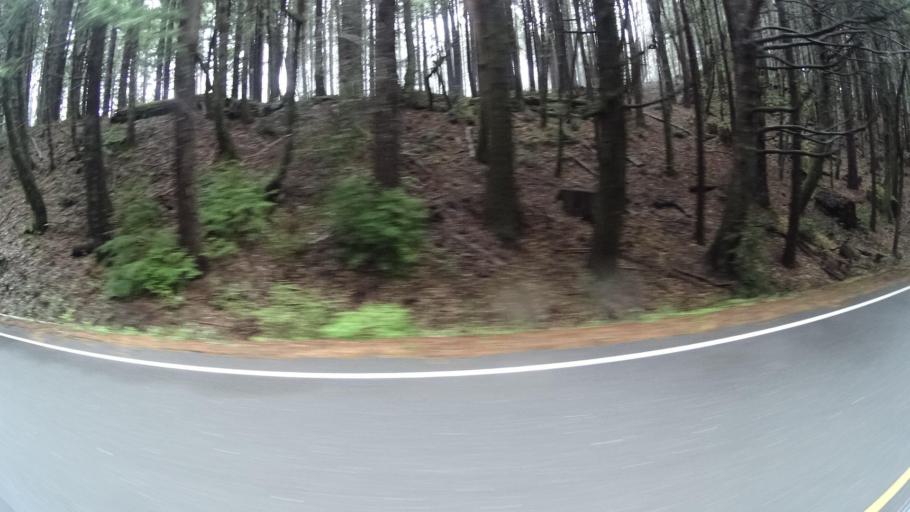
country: US
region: California
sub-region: Humboldt County
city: Westhaven-Moonstone
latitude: 41.2000
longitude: -123.9435
